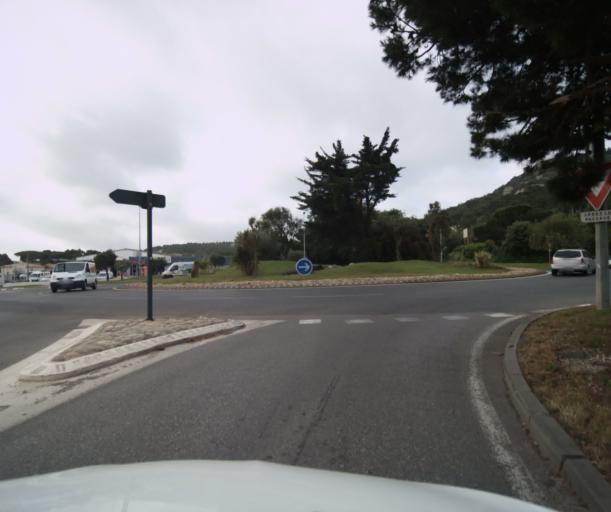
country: FR
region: Provence-Alpes-Cote d'Azur
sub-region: Departement du Var
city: Six-Fours-les-Plages
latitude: 43.1085
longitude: 5.8432
